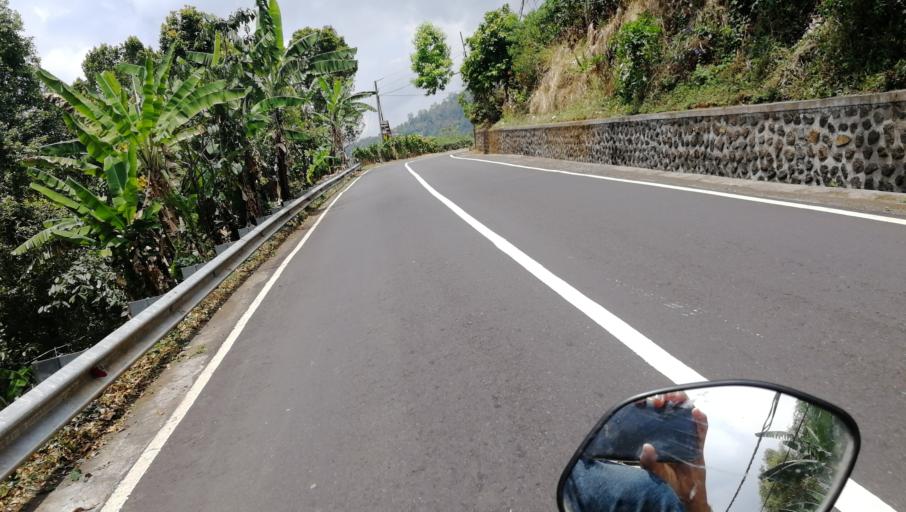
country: ID
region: Bali
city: Munduk
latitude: -8.2604
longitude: 115.0715
